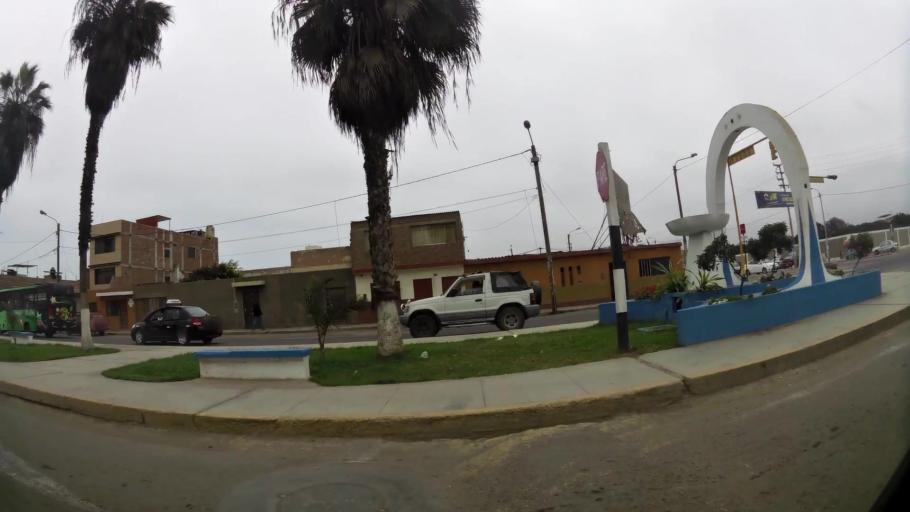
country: PE
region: La Libertad
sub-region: Provincia de Trujillo
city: Buenos Aires
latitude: -8.1409
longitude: -79.0528
